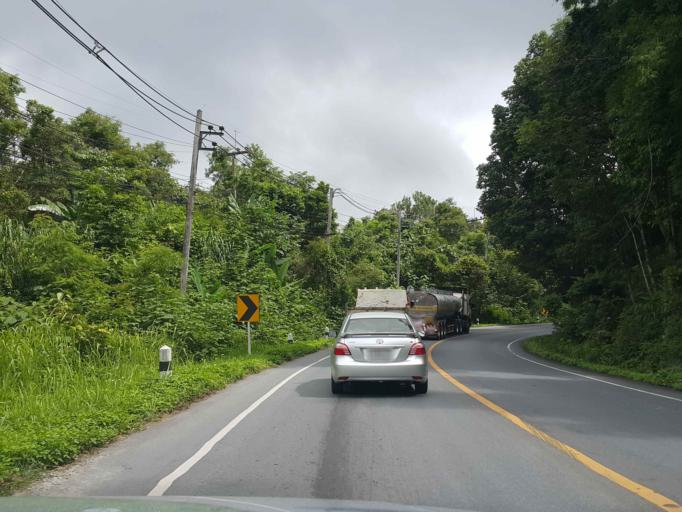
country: TH
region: Tak
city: Tak
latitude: 16.7956
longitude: 98.9513
